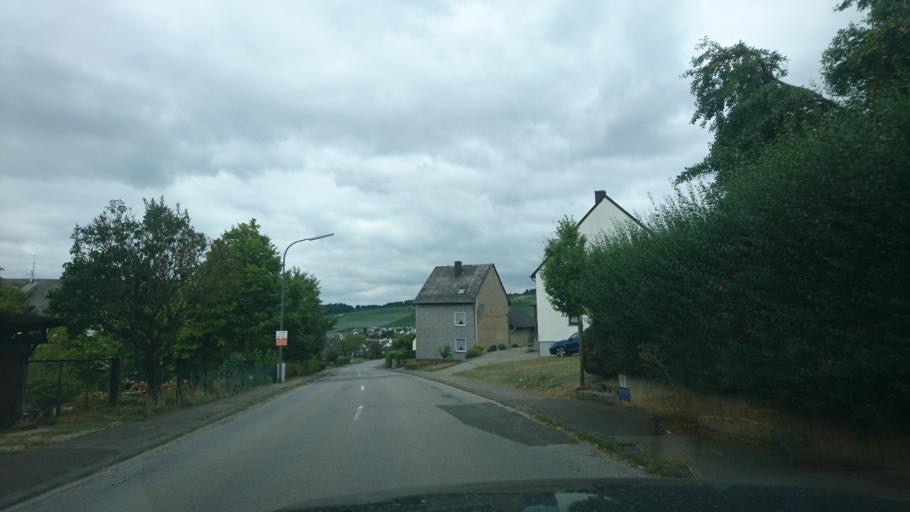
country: DE
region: Rheinland-Pfalz
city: Pellingen
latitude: 49.6892
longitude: 6.6391
